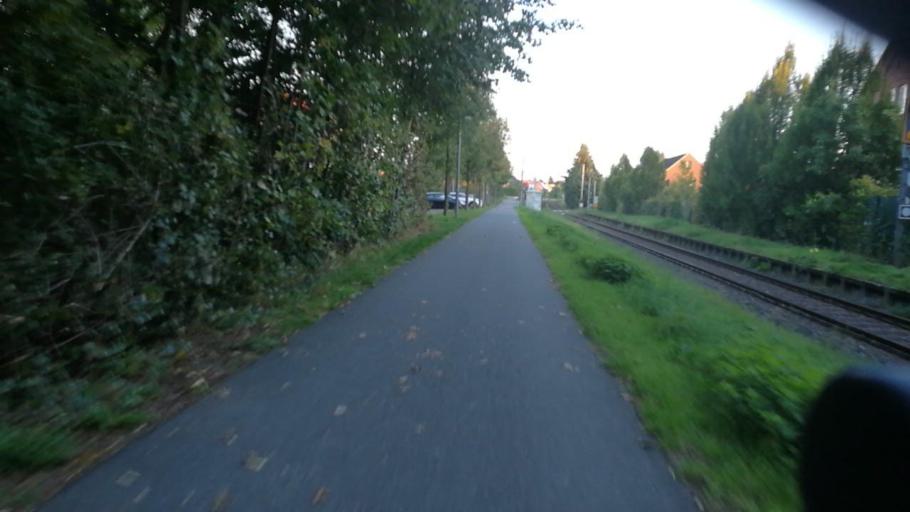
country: DE
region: North Rhine-Westphalia
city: Halle
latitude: 52.0376
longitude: 8.3826
